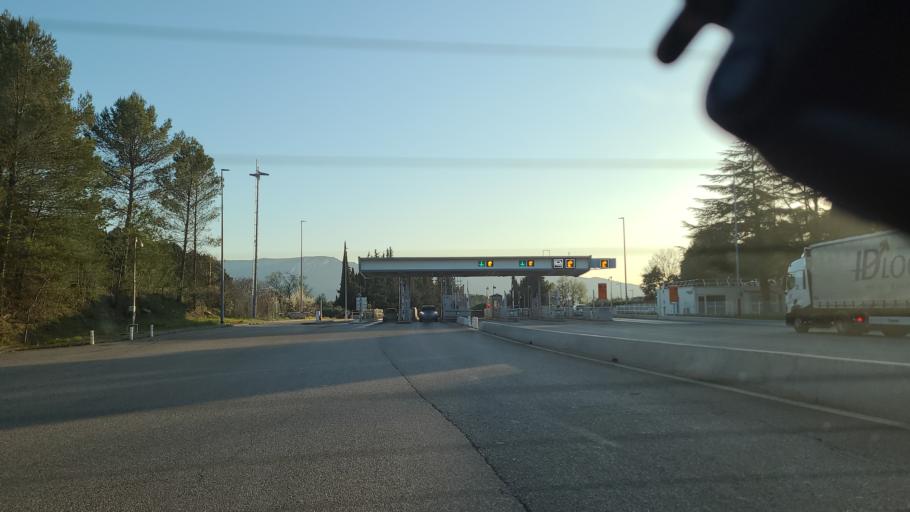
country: FR
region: Provence-Alpes-Cote d'Azur
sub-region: Departement du Var
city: Brignoles
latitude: 43.4197
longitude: 6.0657
